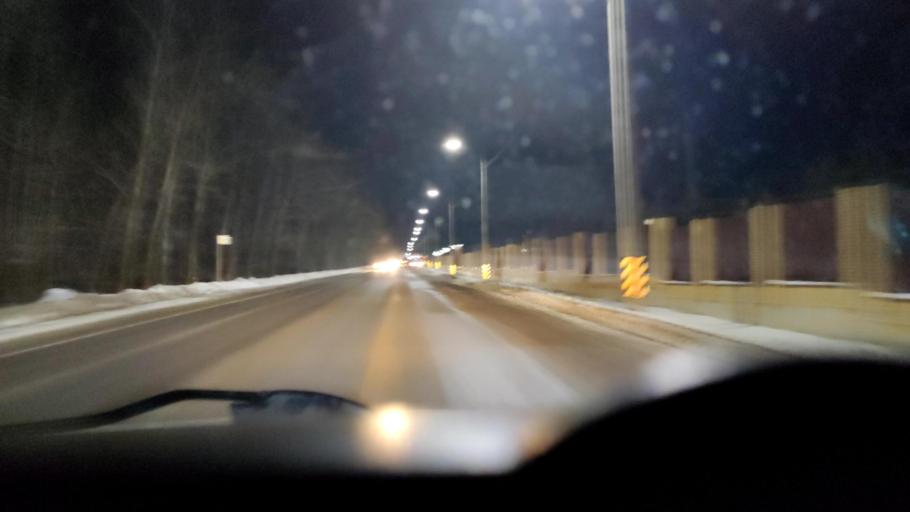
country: RU
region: Voronezj
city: Pridonskoy
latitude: 51.7437
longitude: 39.0519
